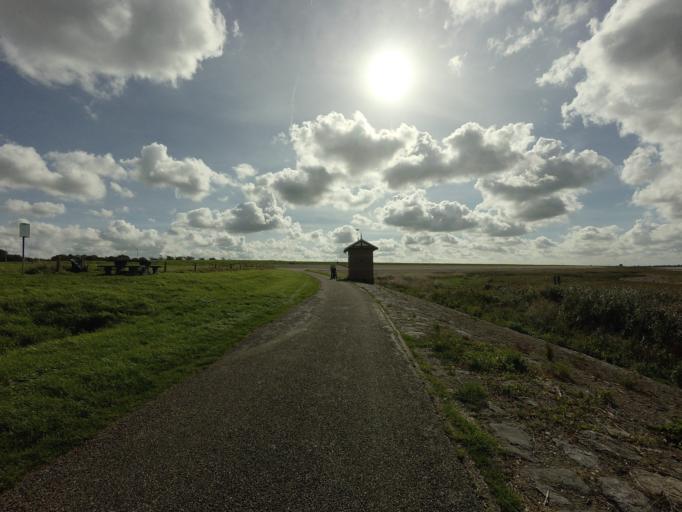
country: NL
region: North Holland
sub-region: Gemeente Hollands Kroon
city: Den Oever
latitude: 52.8941
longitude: 4.9087
